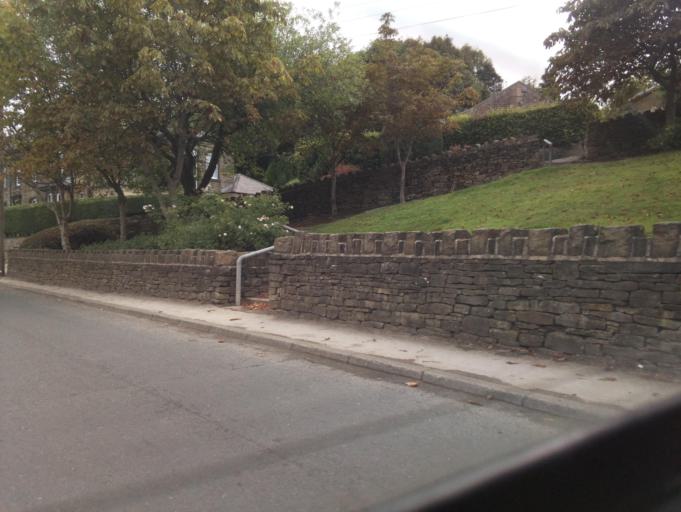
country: GB
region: England
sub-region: Kirklees
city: Holmfirth
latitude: 53.5797
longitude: -1.7762
